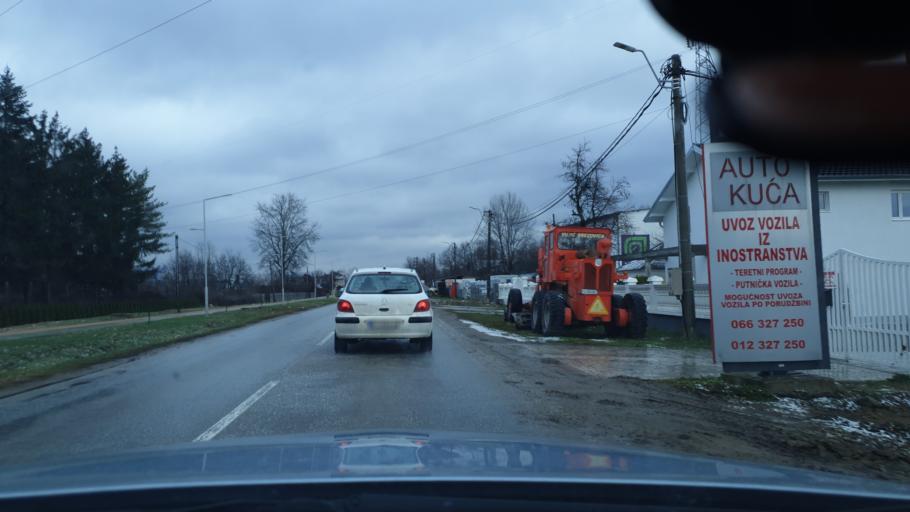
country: RS
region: Central Serbia
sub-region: Branicevski Okrug
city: Petrovac
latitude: 44.3945
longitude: 21.4051
